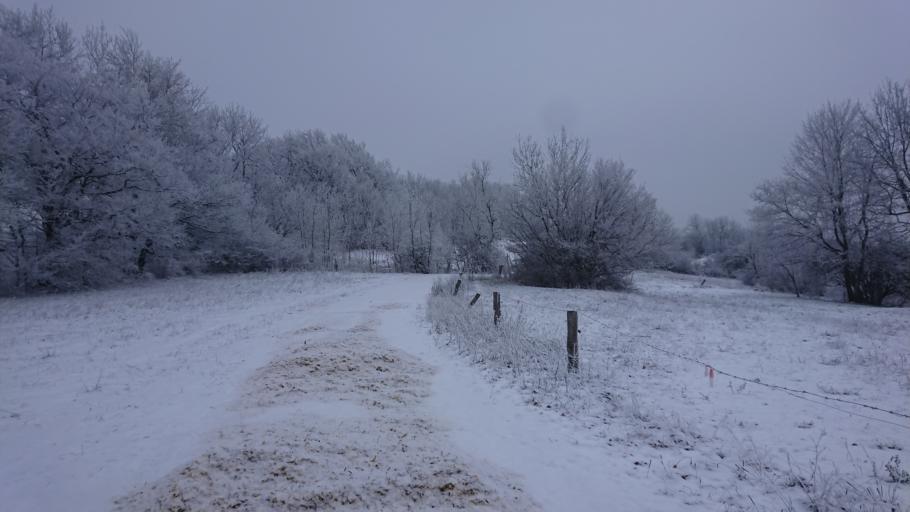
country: DE
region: Thuringia
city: Brehme
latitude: 51.4982
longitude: 10.3851
